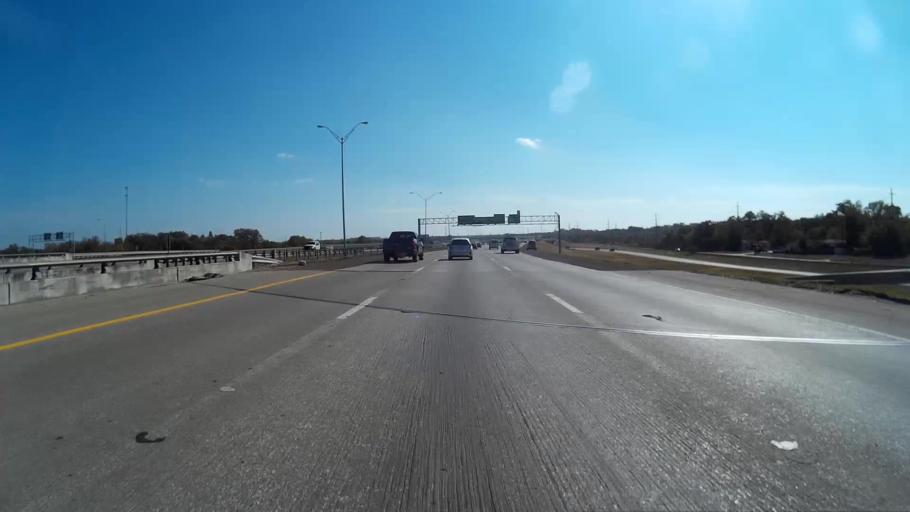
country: US
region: Texas
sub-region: Dallas County
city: Hutchins
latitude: 32.7126
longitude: -96.7564
